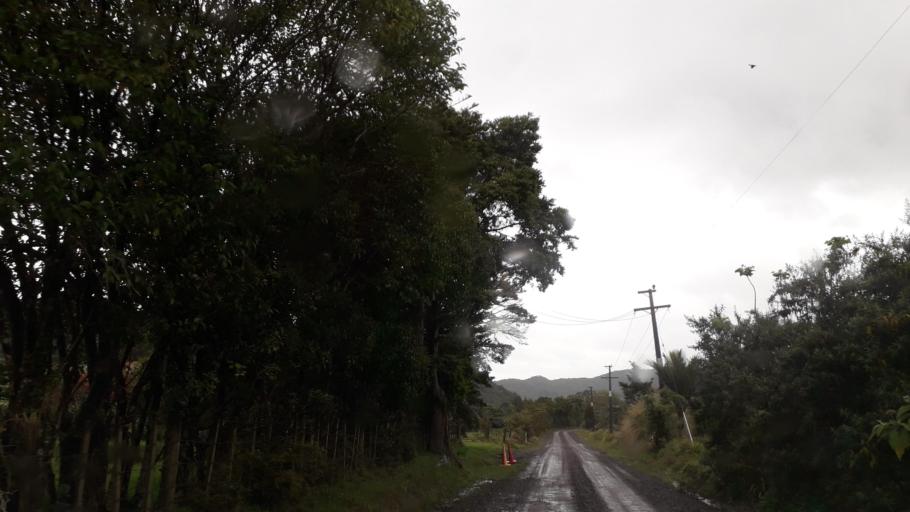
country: NZ
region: Northland
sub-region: Far North District
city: Kaitaia
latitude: -35.3769
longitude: 173.4113
